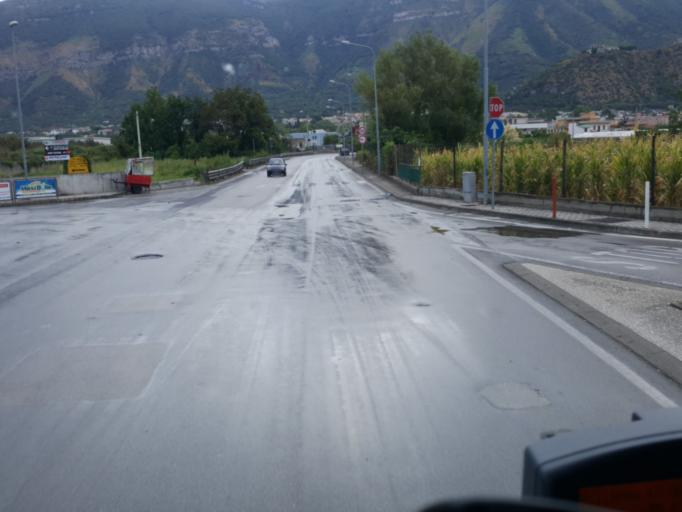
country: IT
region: Campania
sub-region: Provincia di Salerno
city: Sarno
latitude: 40.8136
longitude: 14.6000
